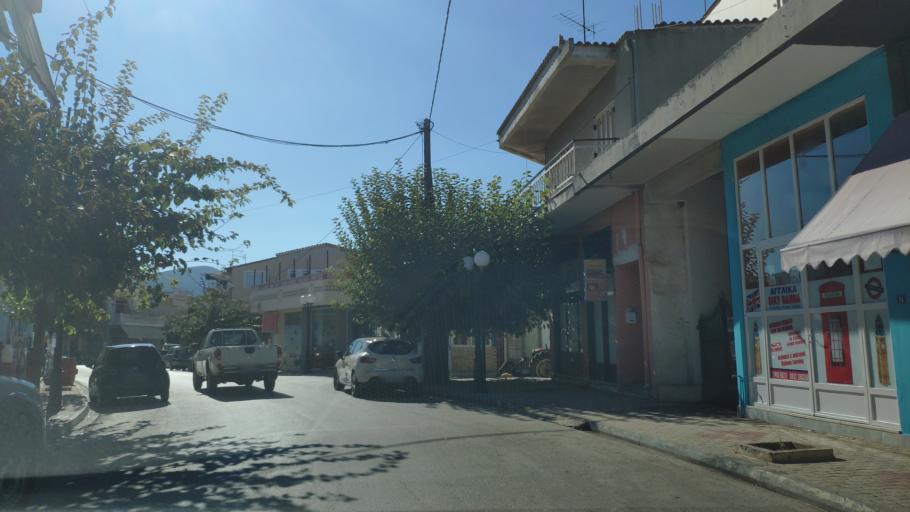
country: GR
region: Peloponnese
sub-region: Nomos Korinthias
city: Khiliomodhi
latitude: 37.8102
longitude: 22.8694
